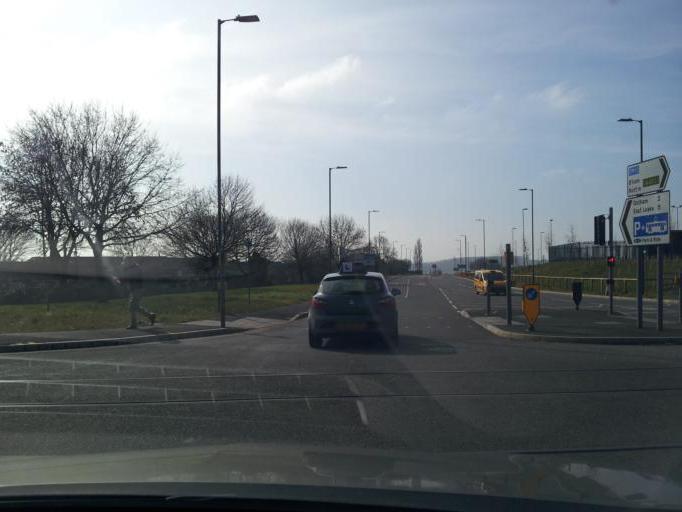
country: GB
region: England
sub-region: Nottinghamshire
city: Gotham
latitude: 52.8974
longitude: -1.1907
